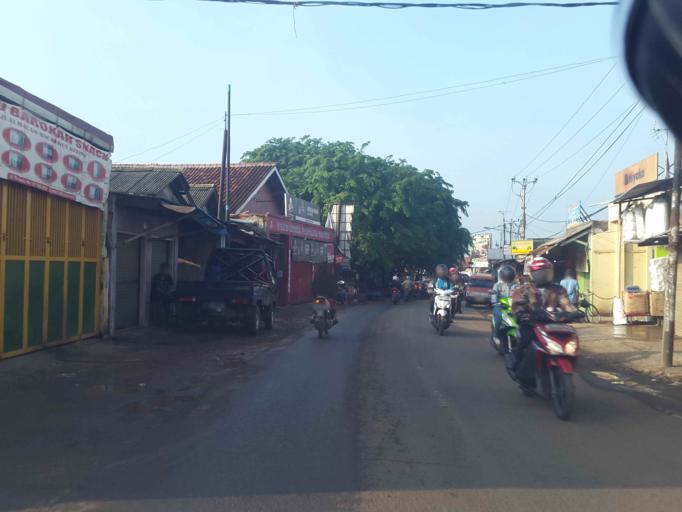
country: ID
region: West Java
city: Cileungsir
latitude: -6.3352
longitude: 107.0457
